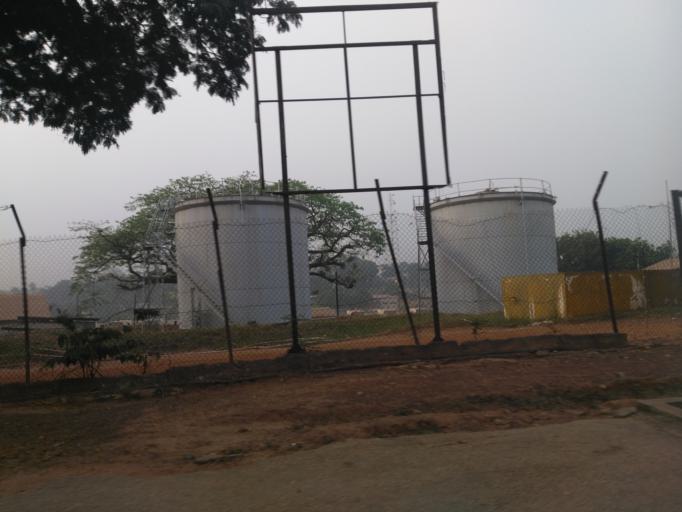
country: GH
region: Ashanti
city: Kumasi
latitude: 6.6816
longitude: -1.6166
